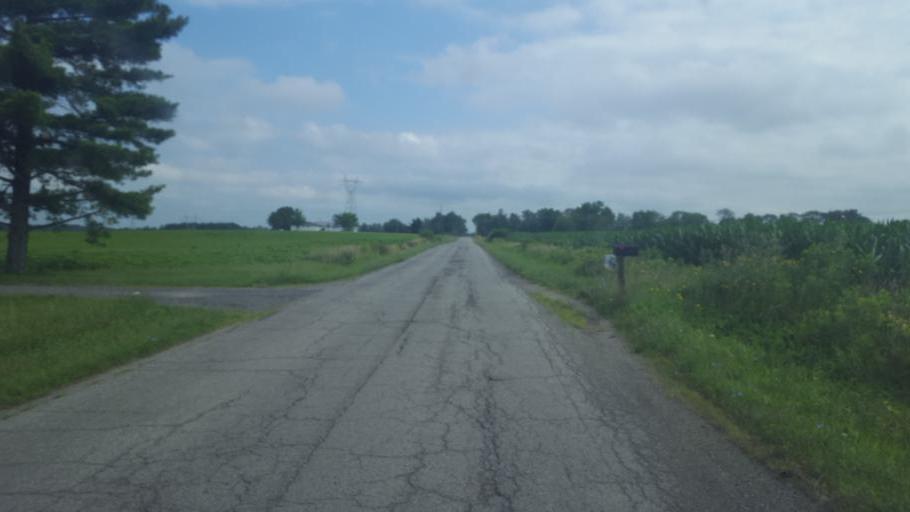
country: US
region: Ohio
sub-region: Crawford County
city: Galion
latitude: 40.6881
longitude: -82.7840
